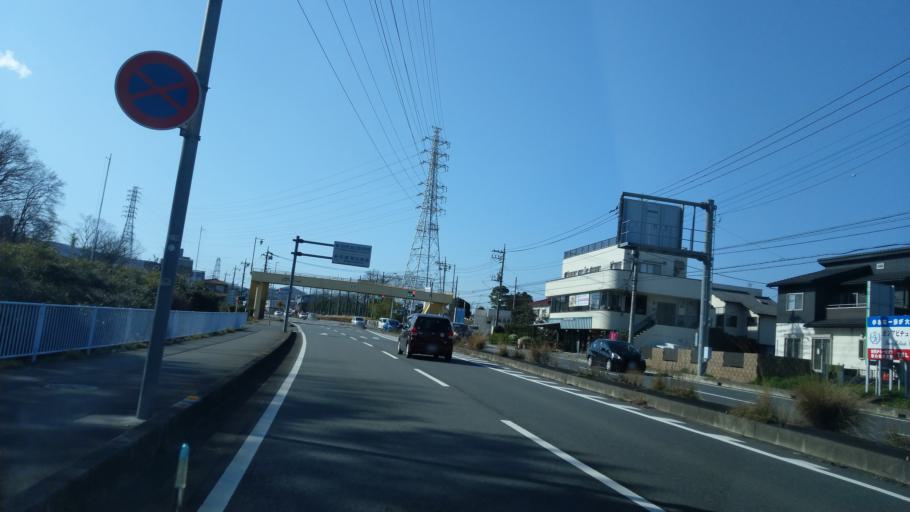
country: JP
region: Saitama
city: Ogawa
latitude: 36.0377
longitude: 139.3241
